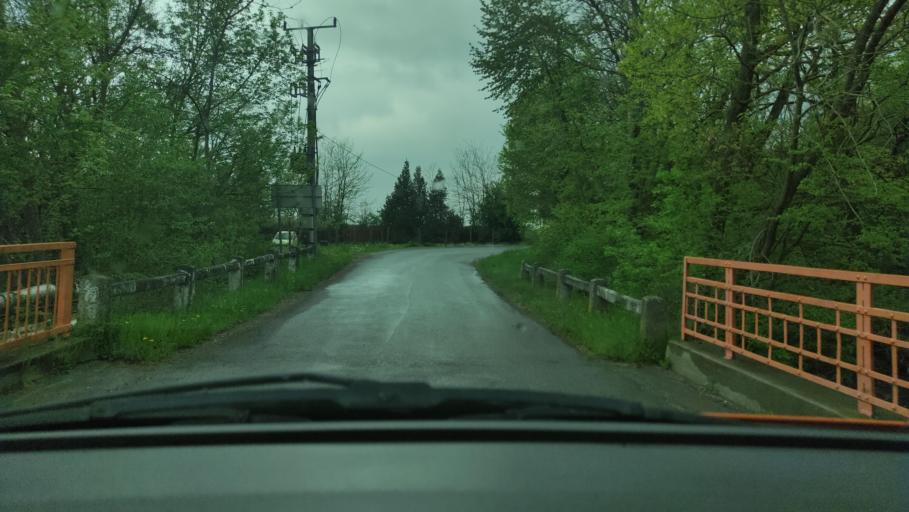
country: HU
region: Baranya
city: Mohacs
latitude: 45.9284
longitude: 18.7065
